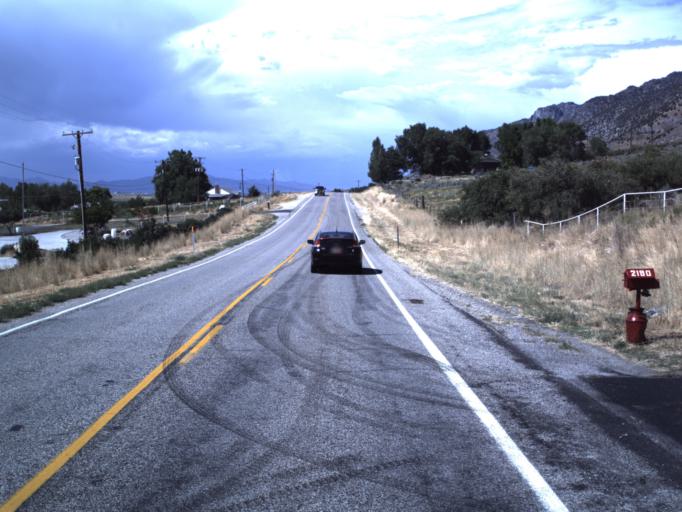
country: US
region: Utah
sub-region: Box Elder County
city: Brigham City
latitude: 41.5495
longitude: -112.0178
